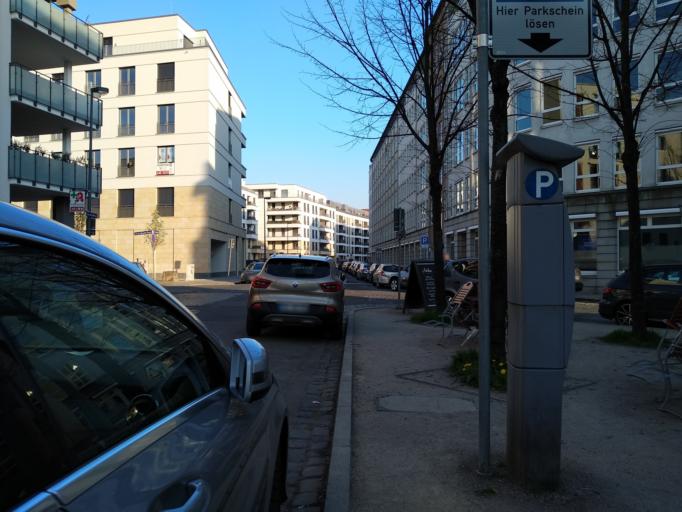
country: DE
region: Saxony
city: Dresden
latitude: 51.0545
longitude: 13.7278
